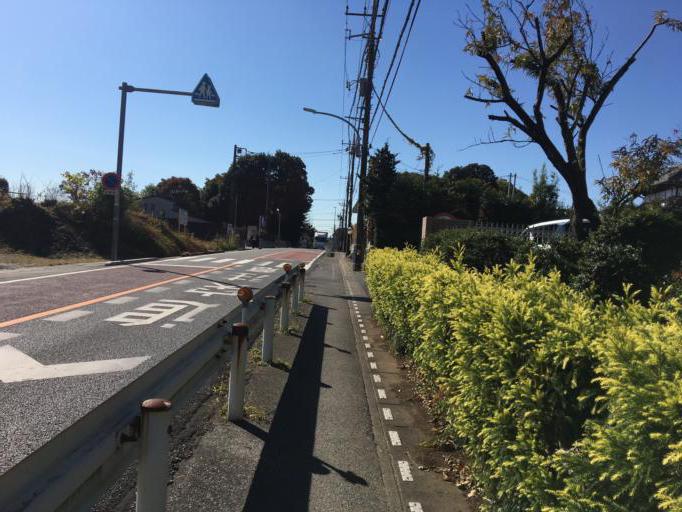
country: JP
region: Saitama
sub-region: Kawaguchi-shi
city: Hatogaya-honcho
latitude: 35.8504
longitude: 139.7507
